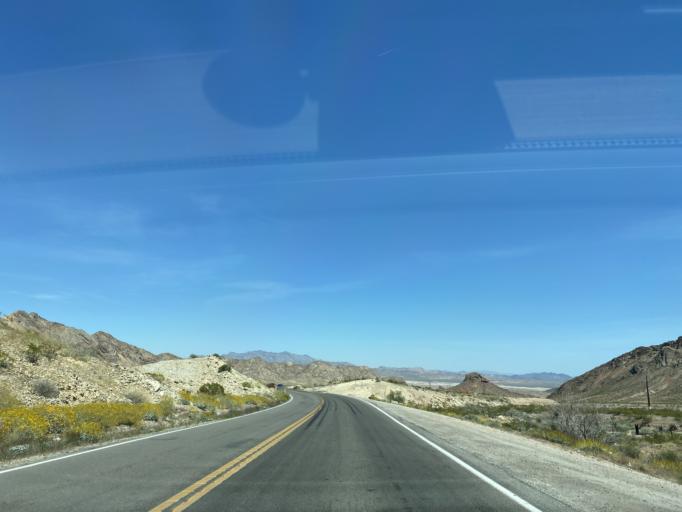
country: US
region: Nevada
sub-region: Clark County
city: Nellis Air Force Base
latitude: 36.2021
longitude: -114.9754
